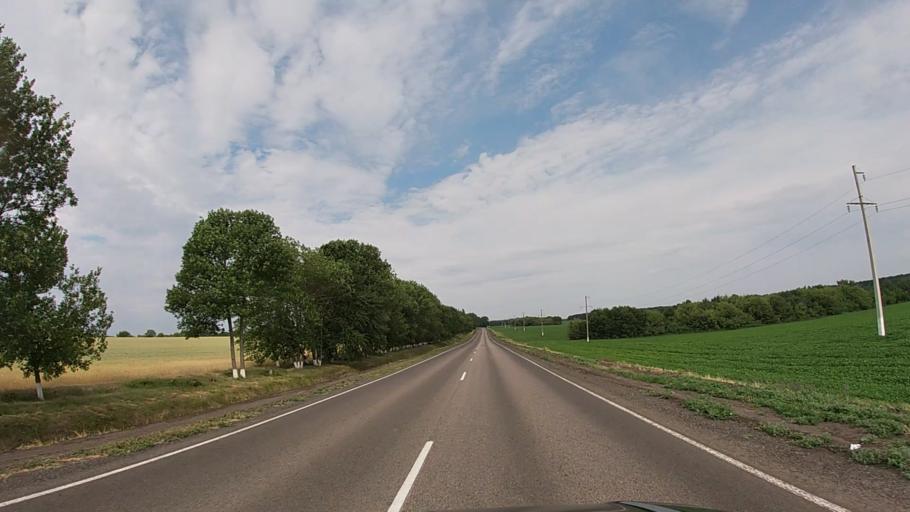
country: RU
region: Belgorod
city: Krasnaya Yaruga
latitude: 50.8095
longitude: 35.5206
